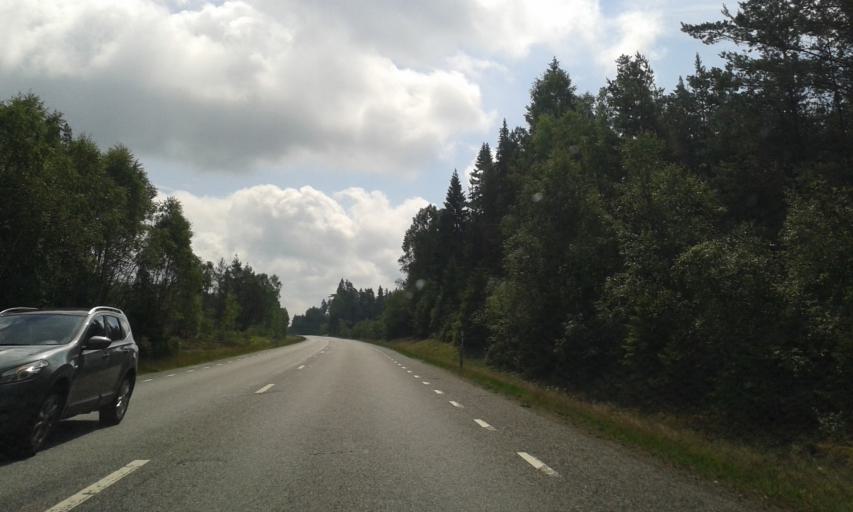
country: SE
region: Vaestra Goetaland
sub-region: Tranemo Kommun
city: Langhem
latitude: 57.5943
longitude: 13.1899
